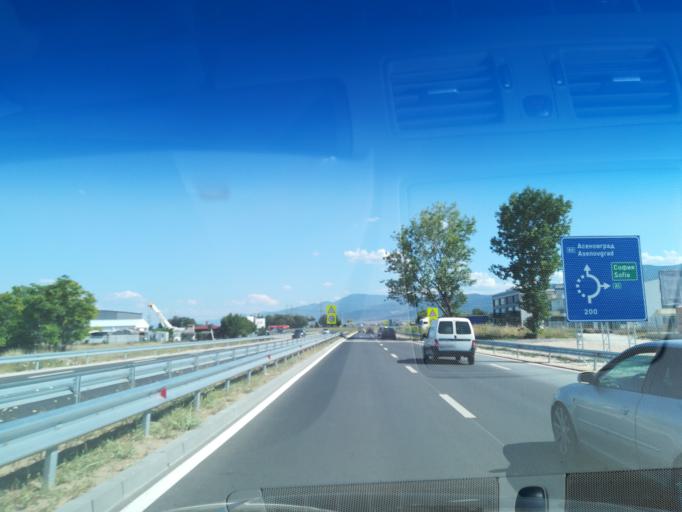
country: BG
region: Plovdiv
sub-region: Obshtina Plovdiv
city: Plovdiv
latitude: 42.1013
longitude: 24.7869
